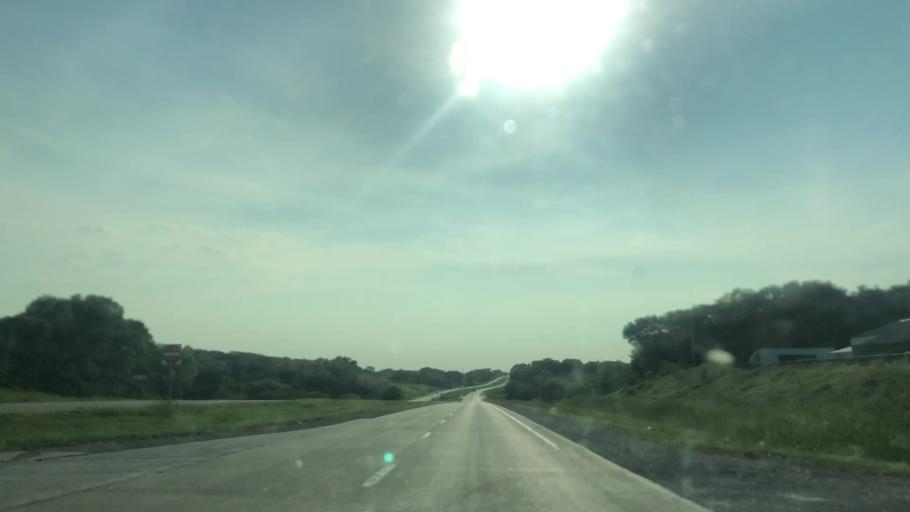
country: US
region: Iowa
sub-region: Story County
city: Nevada
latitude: 42.0079
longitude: -93.3703
